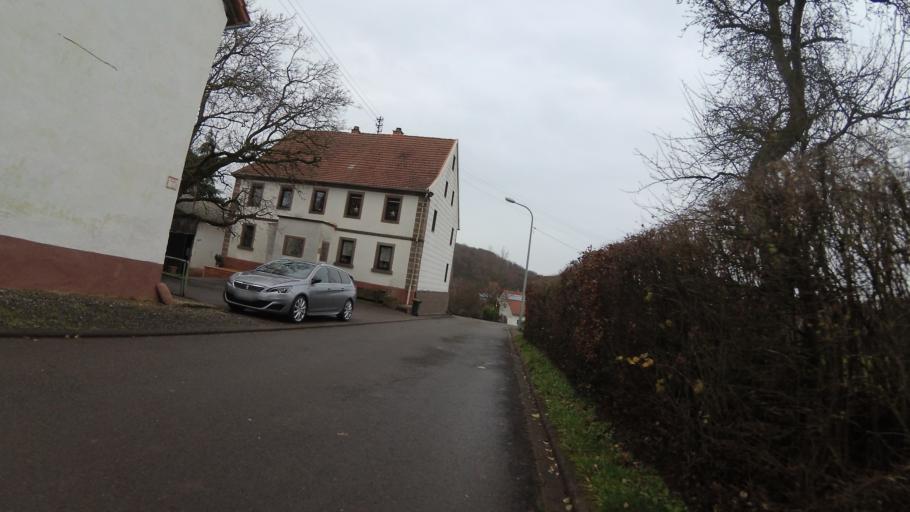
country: DE
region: Rheinland-Pfalz
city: Frohnhofen
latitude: 49.4534
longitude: 7.3033
